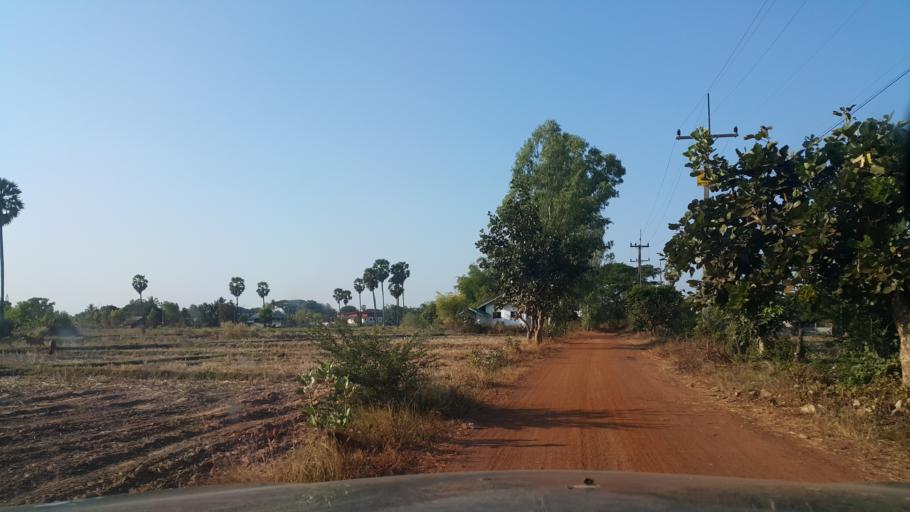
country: TH
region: Changwat Udon Thani
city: Ban Na Muang
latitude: 17.2299
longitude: 103.0437
